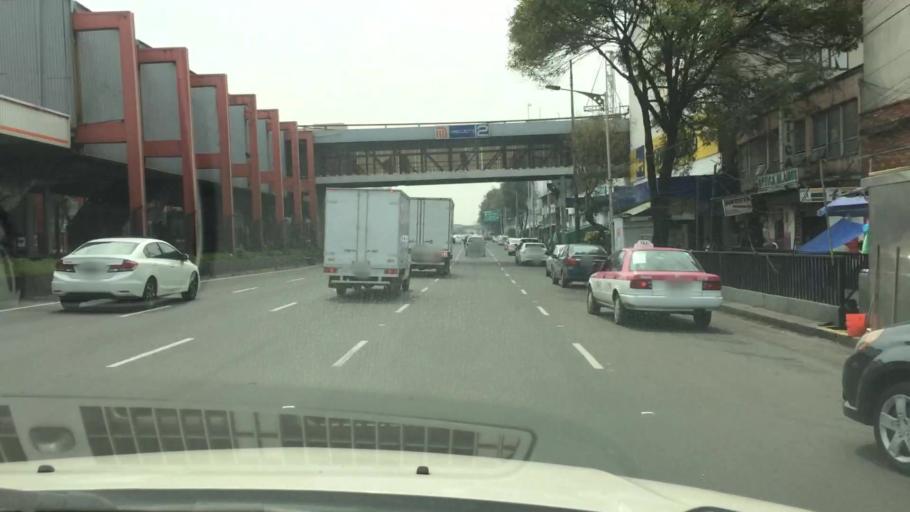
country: MX
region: Mexico City
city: Colonia Nativitas
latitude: 19.4013
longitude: -99.1370
